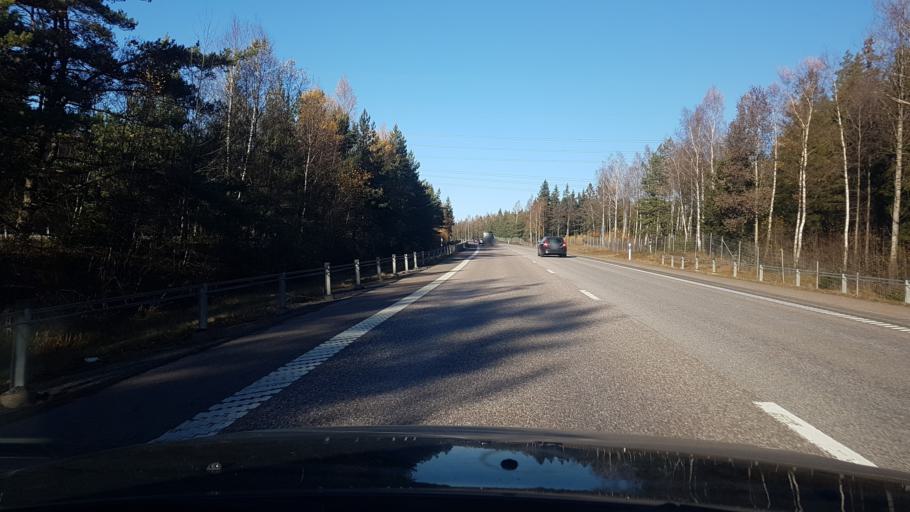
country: SE
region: Stockholm
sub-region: Sigtuna Kommun
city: Marsta
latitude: 59.6912
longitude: 17.8686
